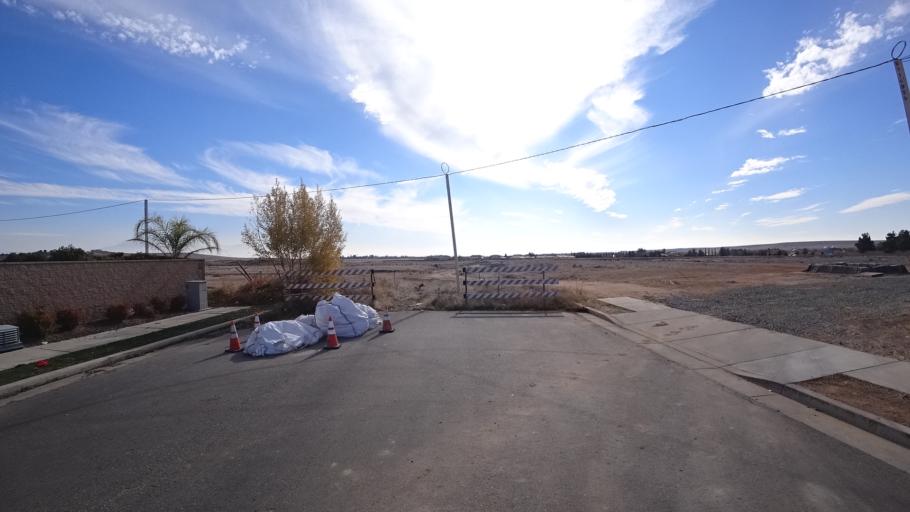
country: US
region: California
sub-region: Kern County
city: Oildale
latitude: 35.4077
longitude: -118.8844
